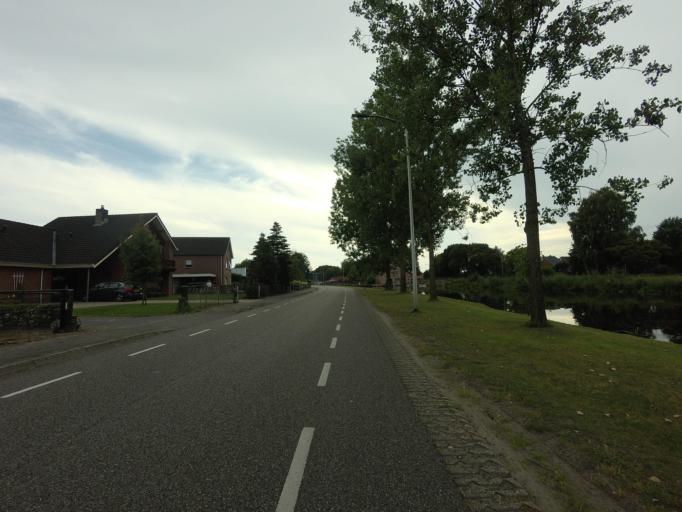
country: DE
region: Lower Saxony
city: Laar
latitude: 52.6128
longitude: 6.6805
